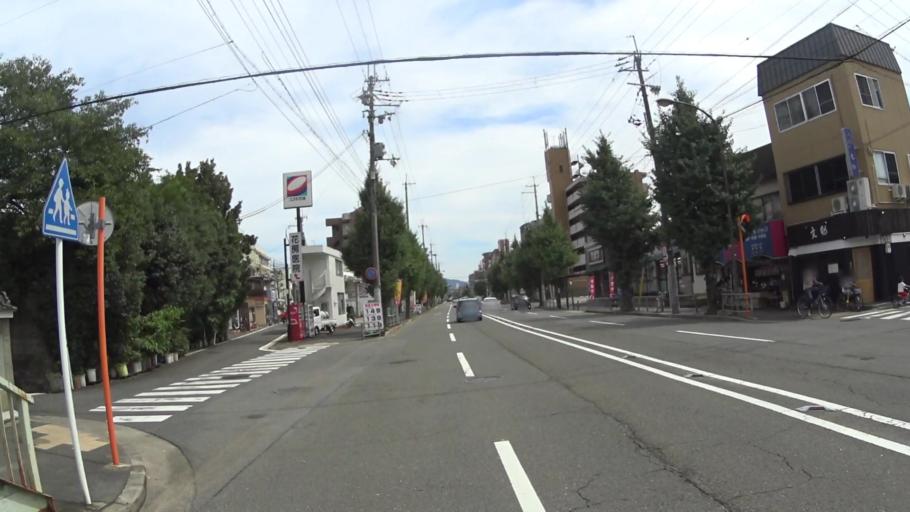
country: JP
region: Kyoto
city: Kyoto
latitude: 35.0196
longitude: 135.7224
